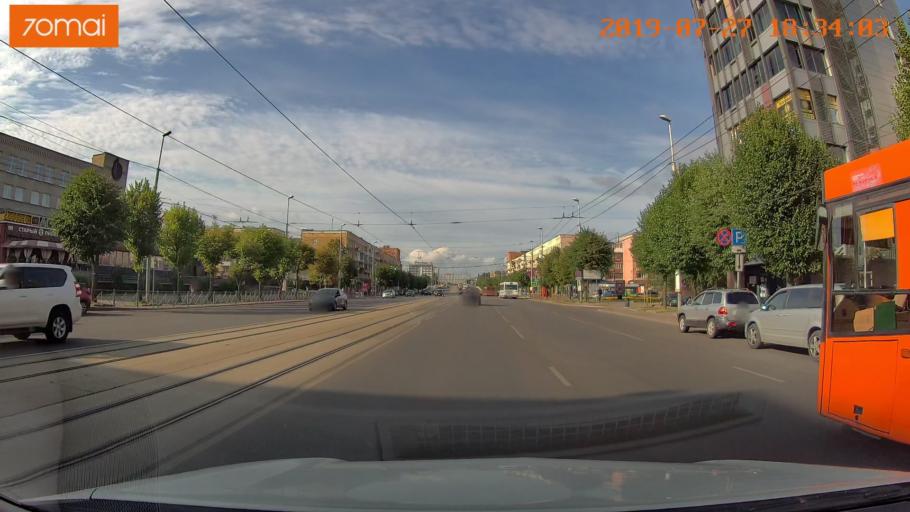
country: RU
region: Kaliningrad
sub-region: Gorod Kaliningrad
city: Kaliningrad
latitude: 54.7015
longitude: 20.5044
